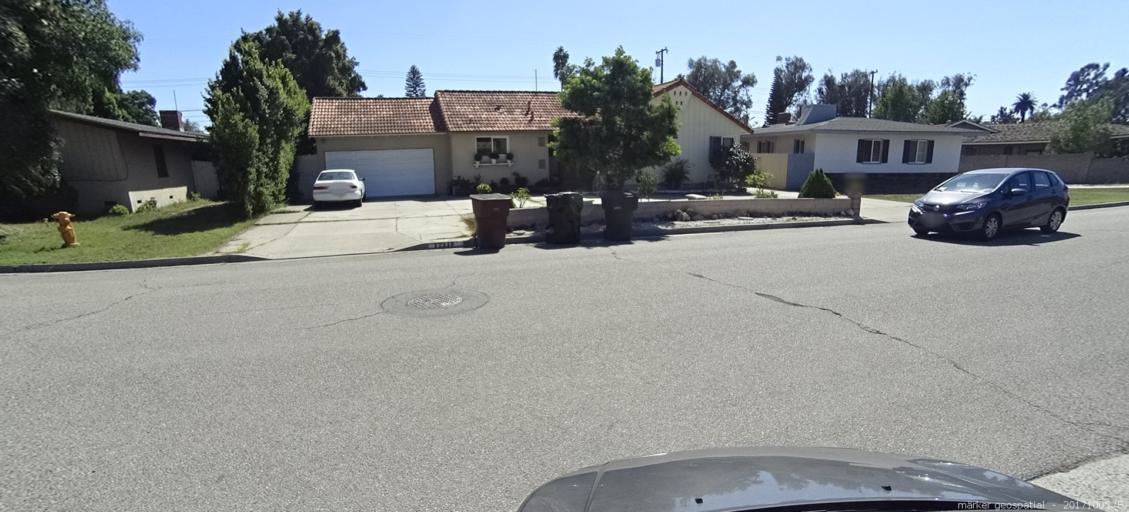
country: US
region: California
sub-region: Orange County
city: Garden Grove
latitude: 33.7822
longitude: -117.9655
